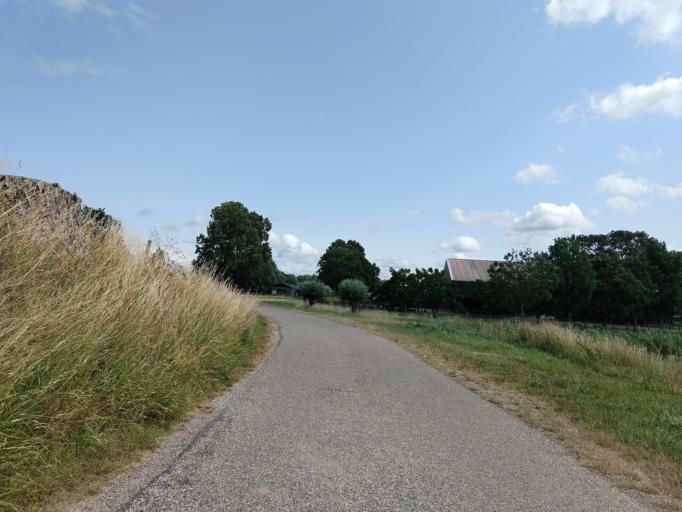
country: NL
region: Zeeland
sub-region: Gemeente Borsele
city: Borssele
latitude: 51.4516
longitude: 3.7971
